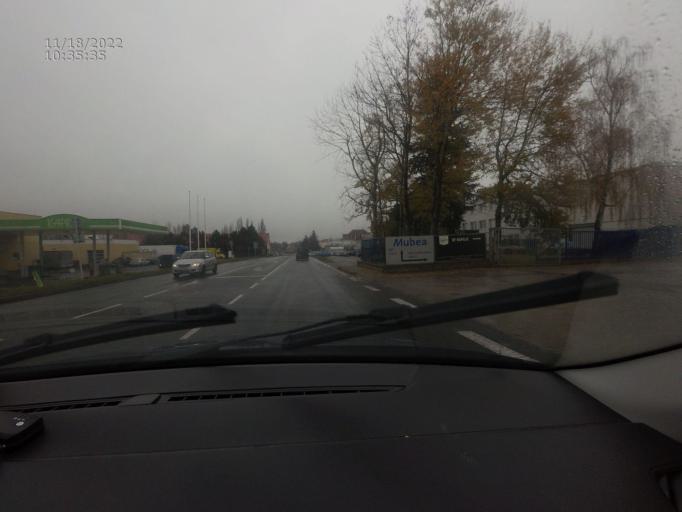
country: CZ
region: Central Bohemia
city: Zebrak
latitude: 49.8698
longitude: 13.8952
